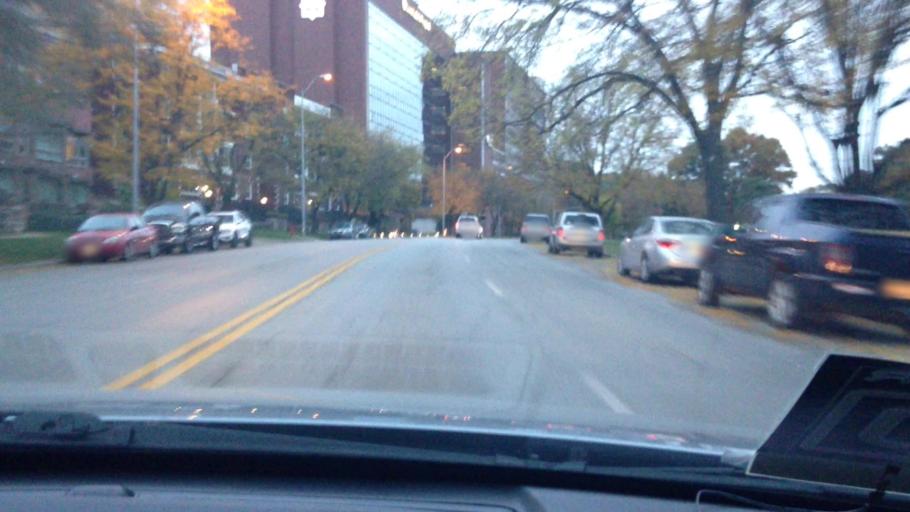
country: US
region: Kansas
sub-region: Johnson County
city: Westwood
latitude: 39.0450
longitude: -94.5888
